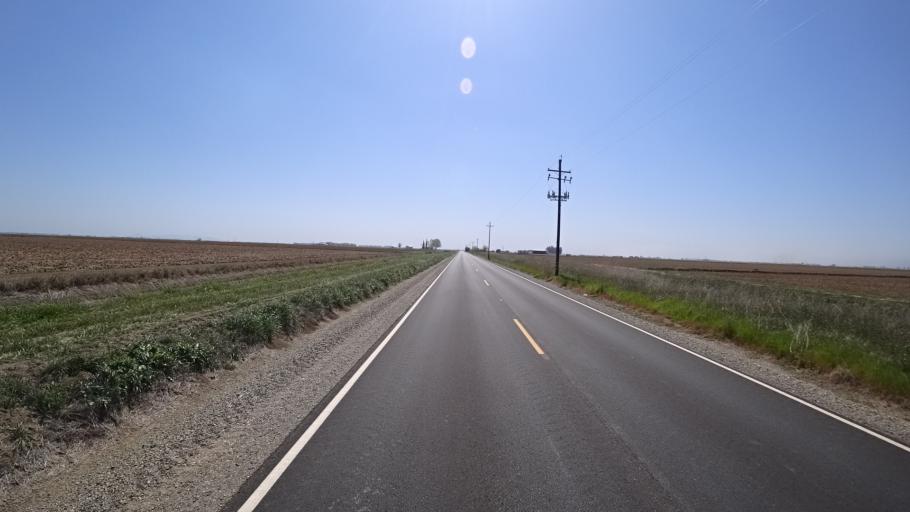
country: US
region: California
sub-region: Glenn County
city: Willows
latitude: 39.4856
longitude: -122.1367
